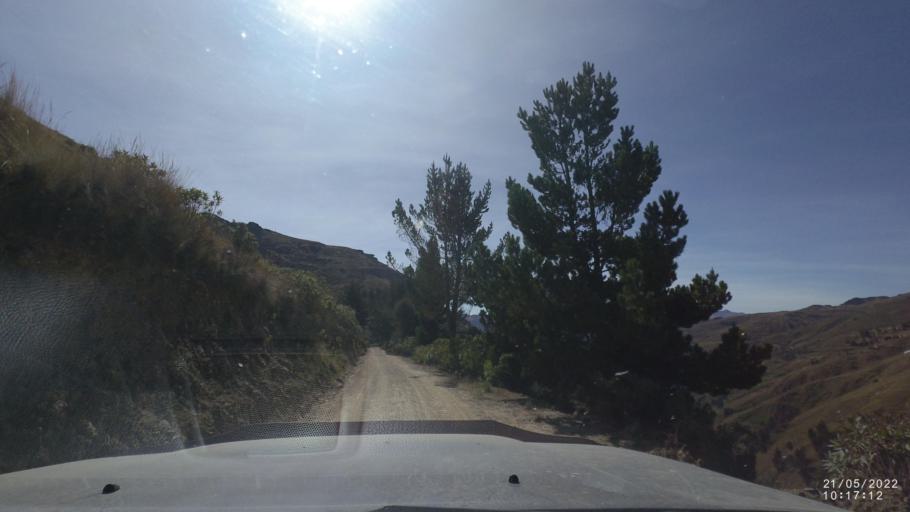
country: BO
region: Cochabamba
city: Colomi
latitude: -17.3302
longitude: -65.9644
